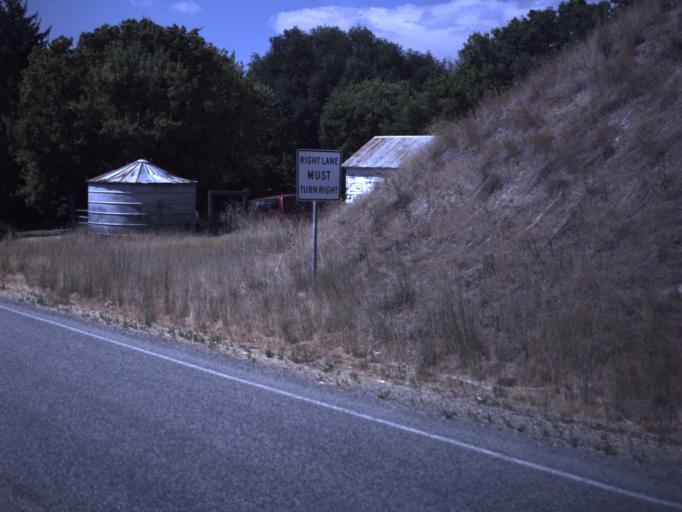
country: US
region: Utah
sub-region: Cache County
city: Mendon
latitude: 41.7946
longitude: -112.0385
